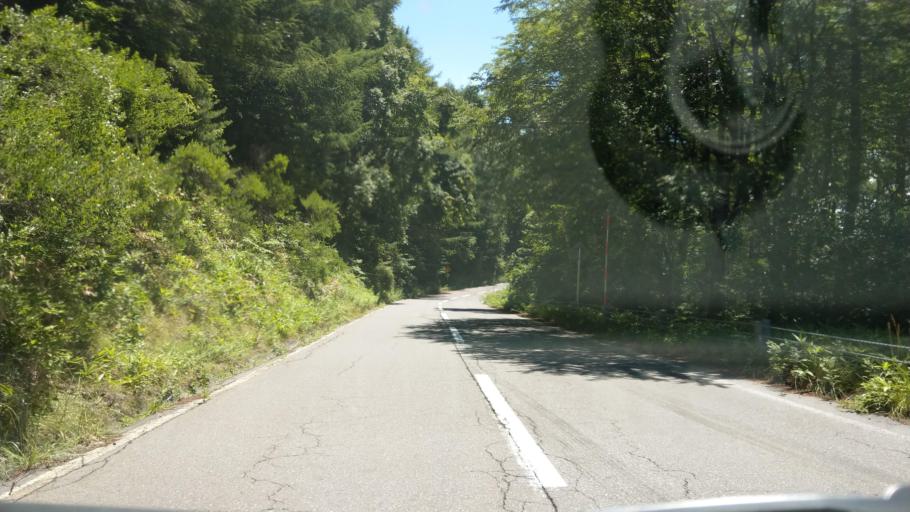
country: JP
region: Nagano
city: Komoro
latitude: 36.3908
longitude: 138.4666
